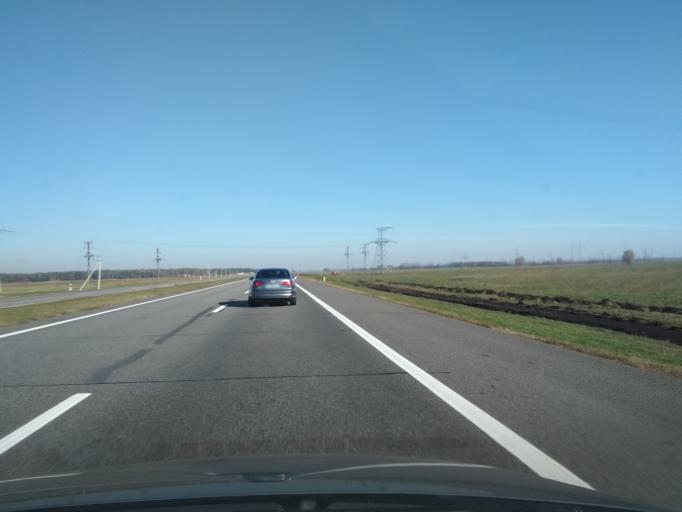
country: BY
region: Brest
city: Antopal'
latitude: 52.4023
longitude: 24.7956
